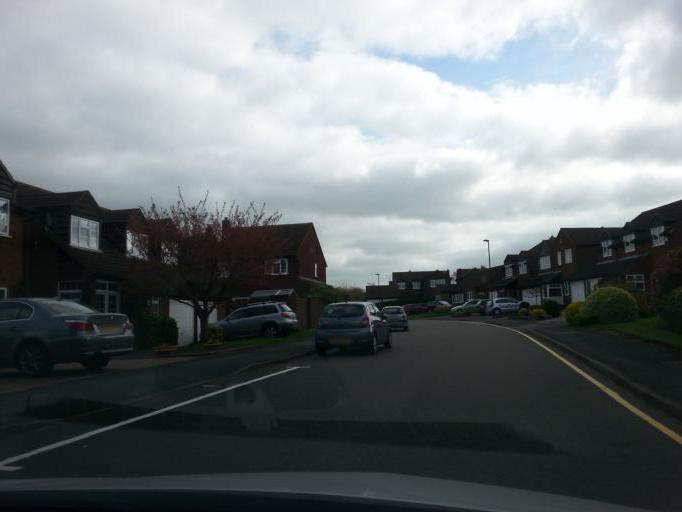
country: GB
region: England
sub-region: Staffordshire
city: Shenstone
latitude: 52.6047
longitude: -1.8434
